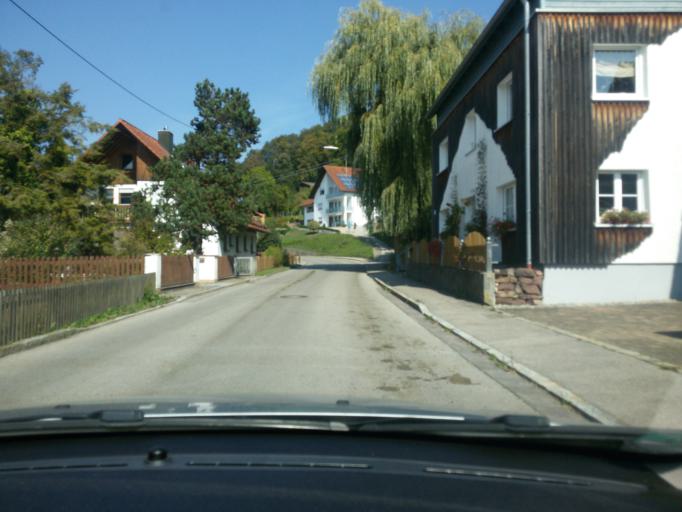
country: DE
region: Bavaria
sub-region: Swabia
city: Walkertshofen
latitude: 48.2251
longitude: 10.5931
